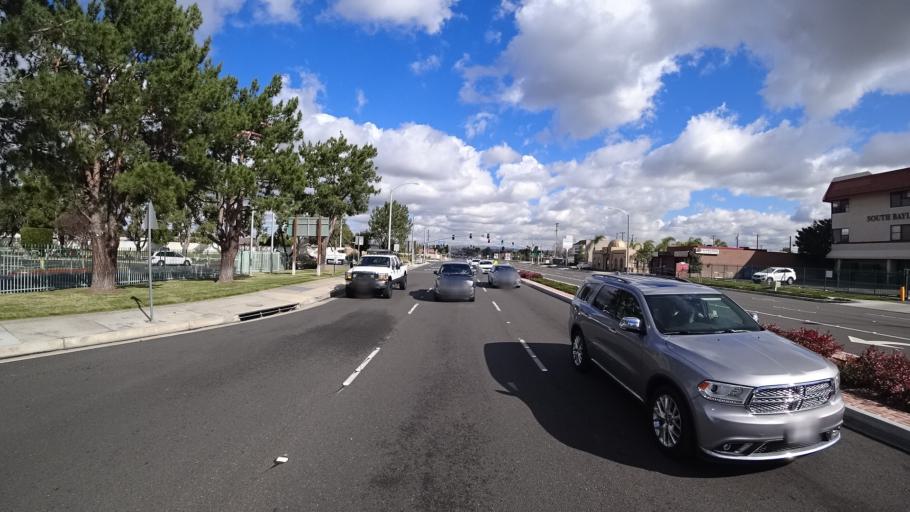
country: US
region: California
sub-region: Orange County
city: Fullerton
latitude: 33.8480
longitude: -117.9593
